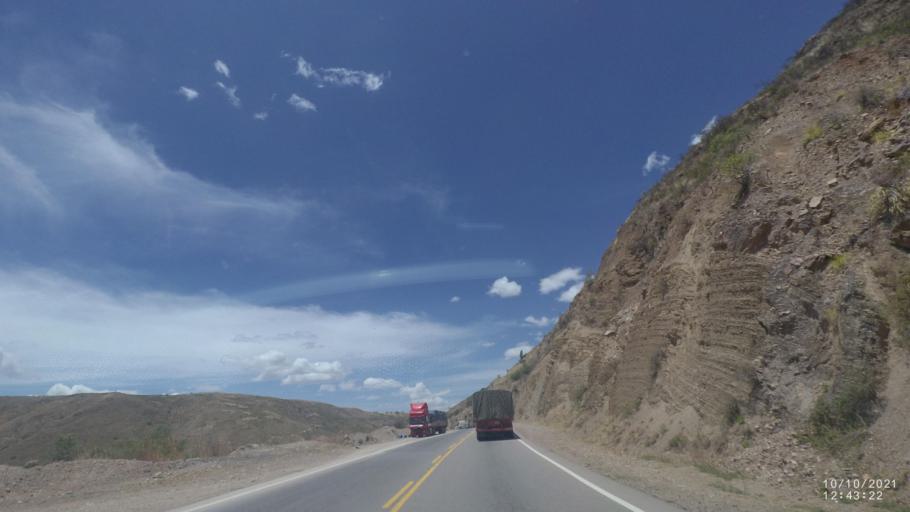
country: BO
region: Cochabamba
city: Irpa Irpa
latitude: -17.6300
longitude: -66.3857
